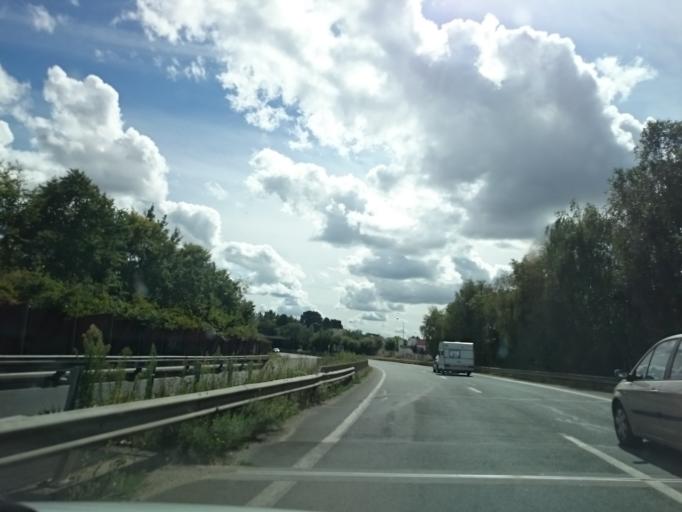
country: FR
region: Pays de la Loire
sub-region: Departement de la Loire-Atlantique
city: Basse-Goulaine
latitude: 47.2121
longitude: -1.4844
